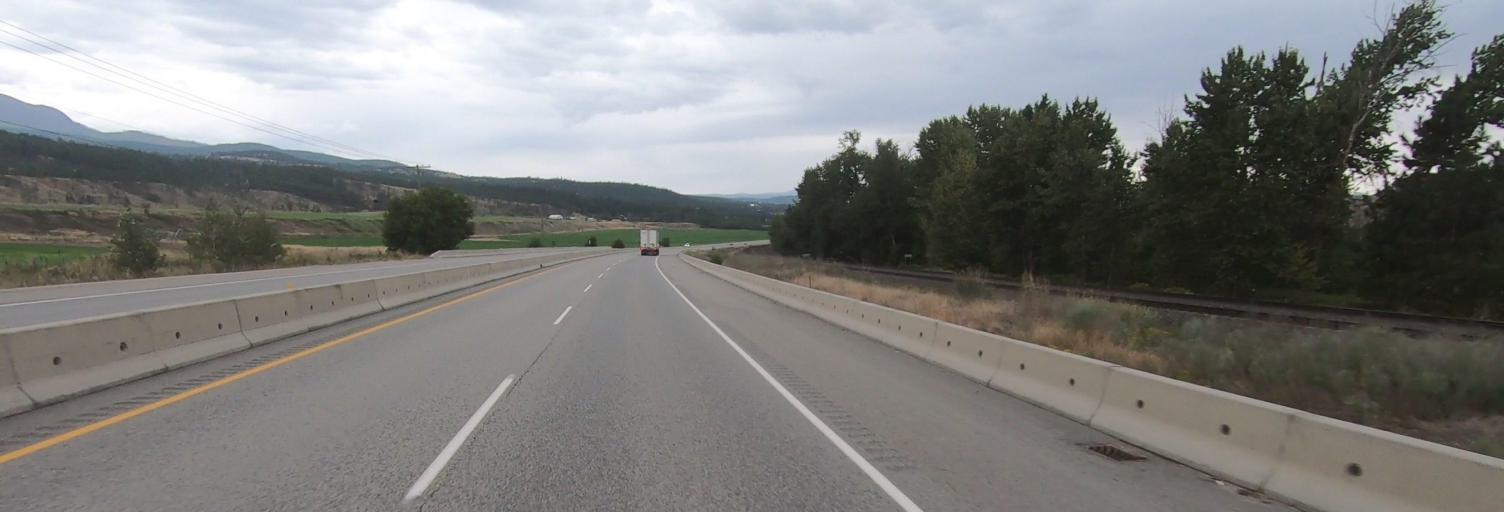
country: CA
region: British Columbia
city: Chase
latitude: 50.7065
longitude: -119.7922
